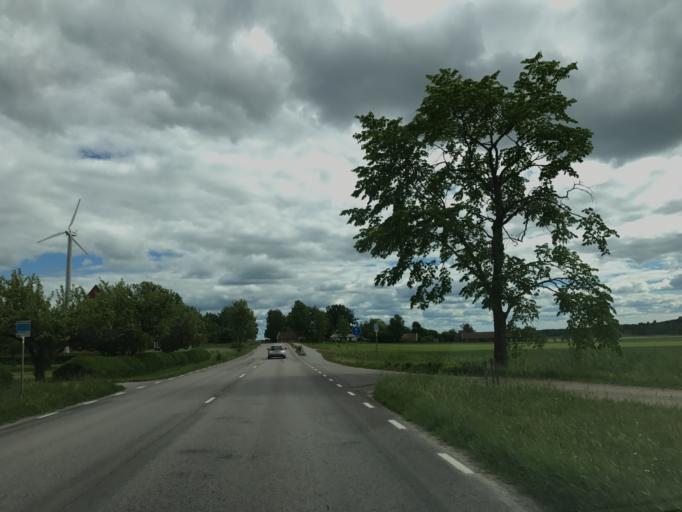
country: SE
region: OErebro
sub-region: Orebro Kommun
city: Orebro
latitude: 59.3172
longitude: 15.1413
